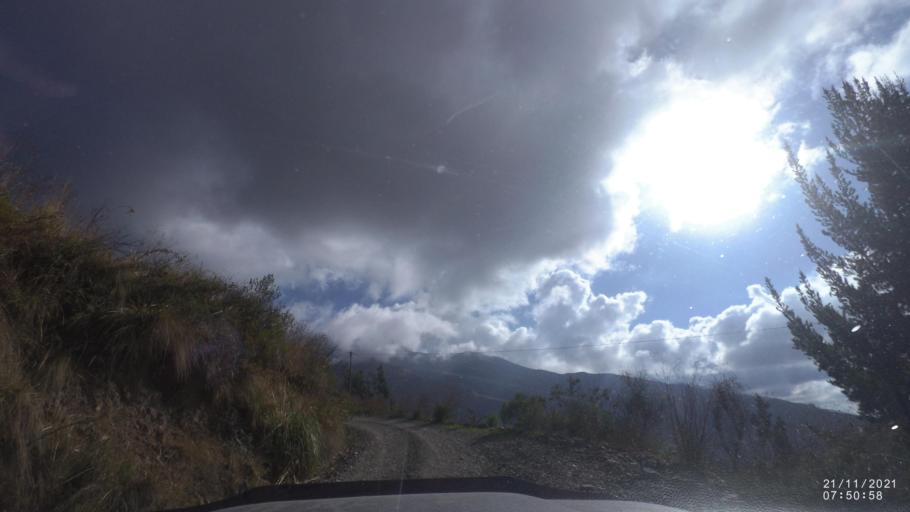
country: BO
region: Cochabamba
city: Cochabamba
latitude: -17.3074
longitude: -66.2171
